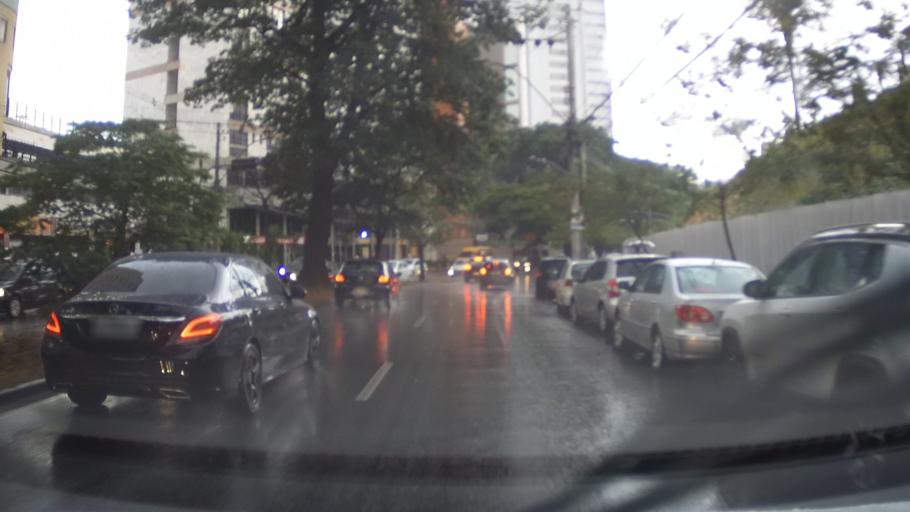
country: BR
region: Minas Gerais
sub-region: Belo Horizonte
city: Belo Horizonte
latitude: -19.9442
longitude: -43.9568
